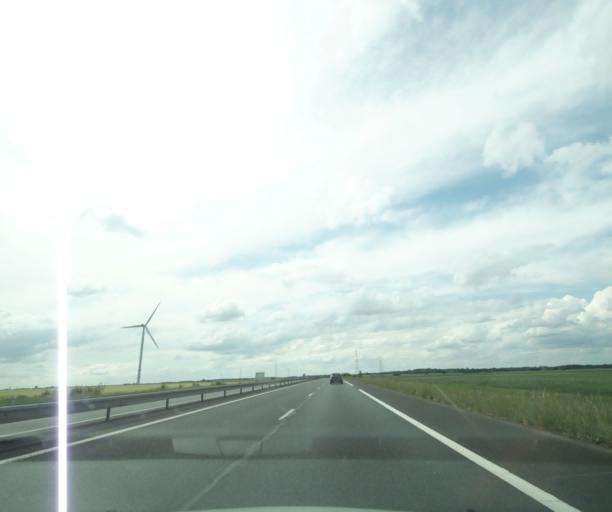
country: FR
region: Centre
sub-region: Departement du Cher
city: Mehun-sur-Yevre
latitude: 47.1000
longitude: 2.2275
